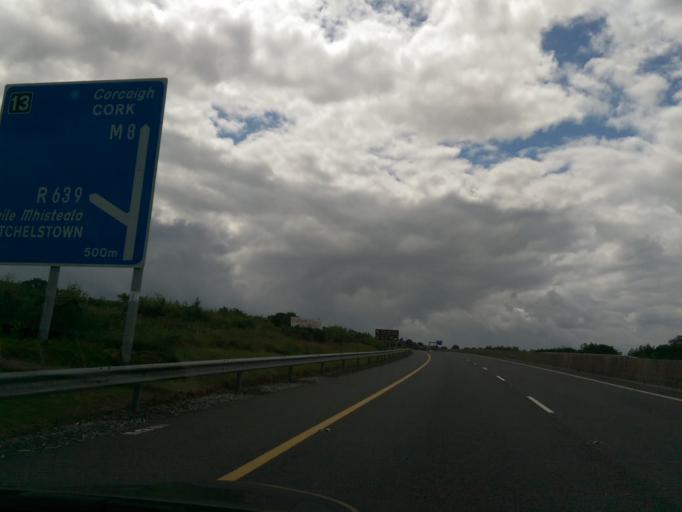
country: IE
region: Munster
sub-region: County Cork
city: Mitchelstown
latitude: 52.2452
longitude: -8.2692
